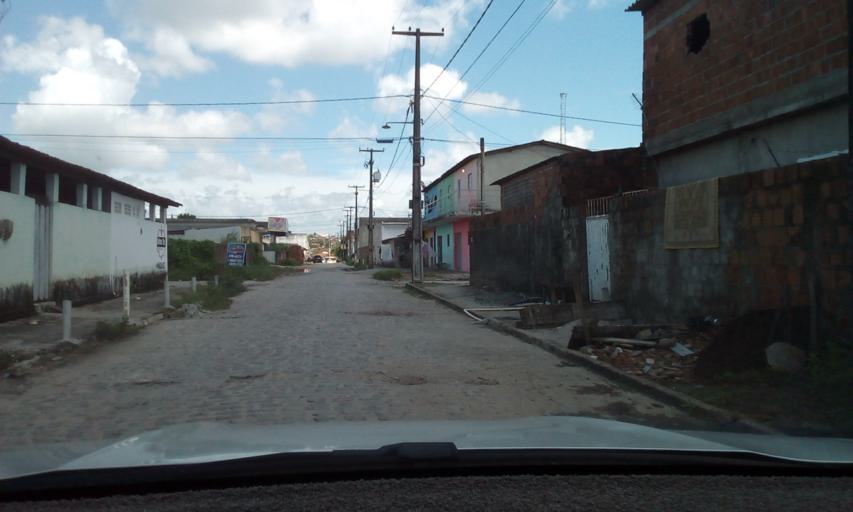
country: BR
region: Paraiba
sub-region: Bayeux
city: Bayeux
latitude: -7.1190
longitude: -34.9373
